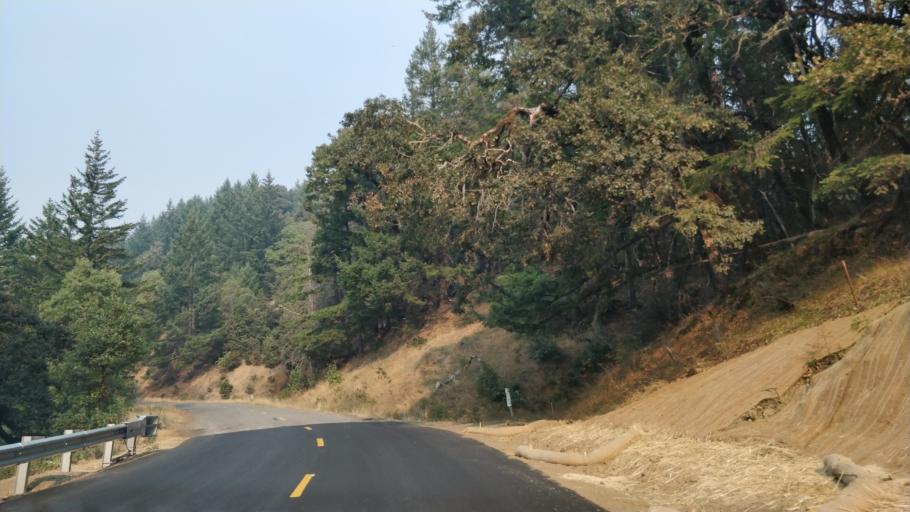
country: US
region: California
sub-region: Humboldt County
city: Rio Dell
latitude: 40.2619
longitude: -124.0957
